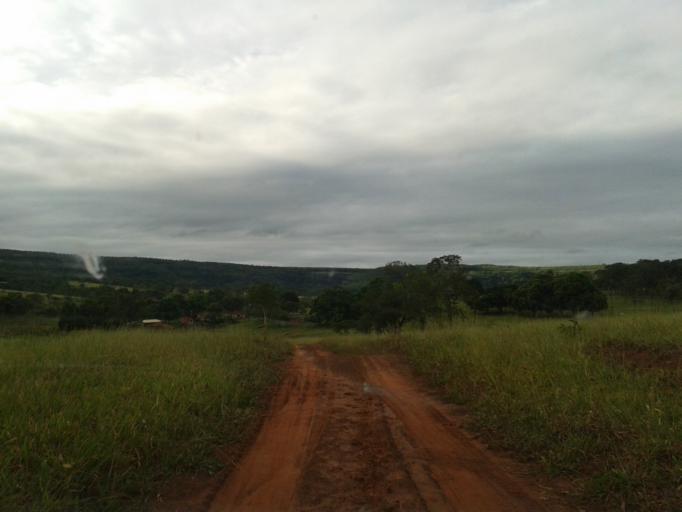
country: BR
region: Minas Gerais
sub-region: Campina Verde
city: Campina Verde
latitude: -19.4729
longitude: -49.6363
